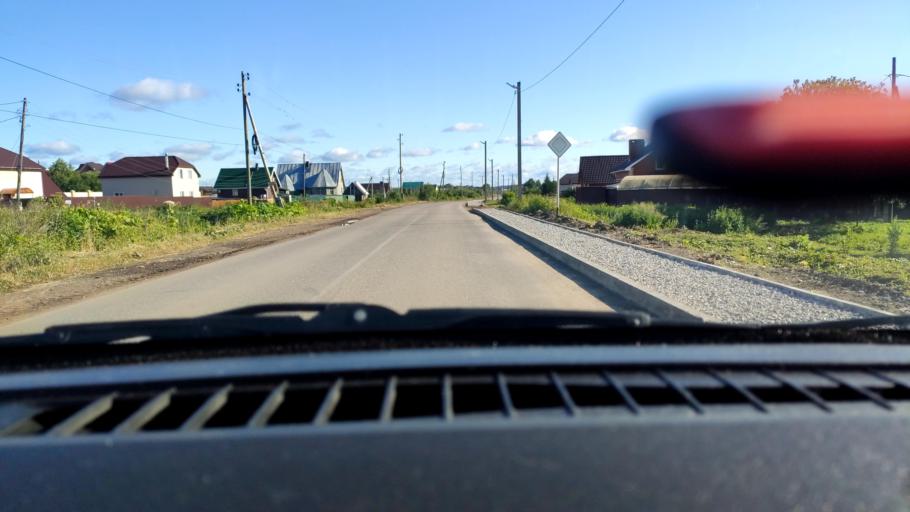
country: RU
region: Perm
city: Kultayevo
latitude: 57.8665
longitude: 55.9159
